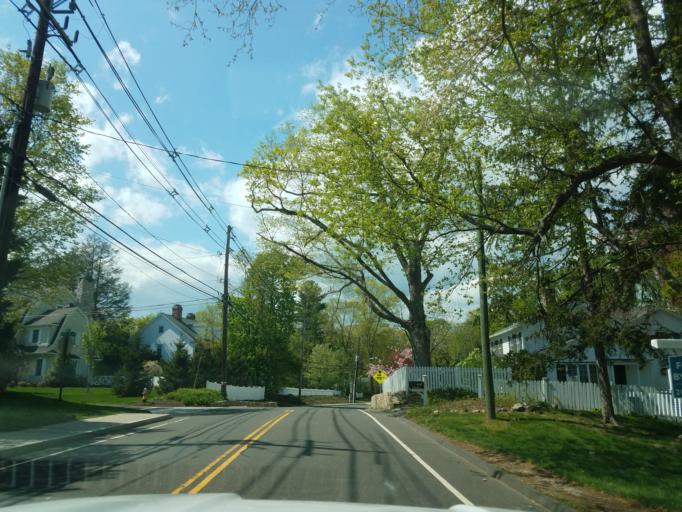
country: US
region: Connecticut
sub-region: Fairfield County
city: New Canaan
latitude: 41.1386
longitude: -73.4824
